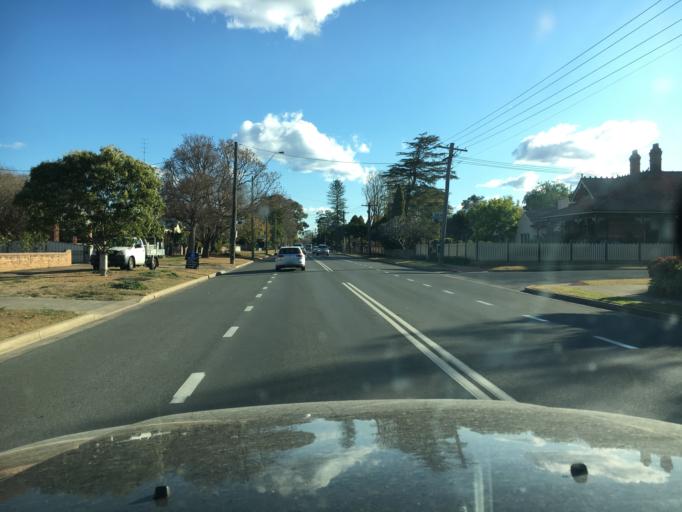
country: AU
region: New South Wales
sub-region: Maitland Municipality
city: Maitland
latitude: -32.7255
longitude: 151.5621
